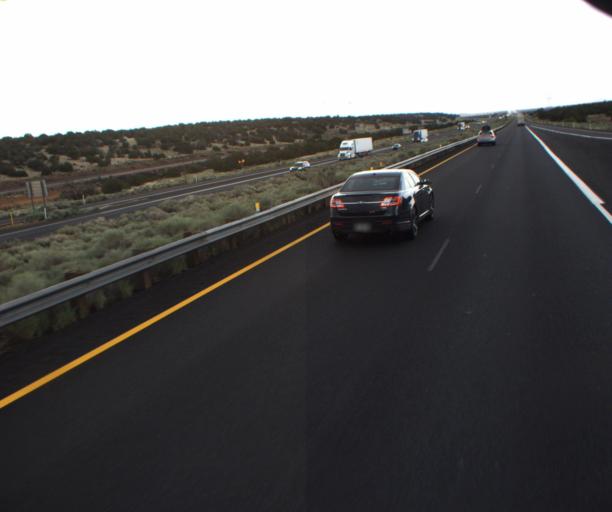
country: US
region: Arizona
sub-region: Coconino County
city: Flagstaff
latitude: 35.2004
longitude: -111.4041
